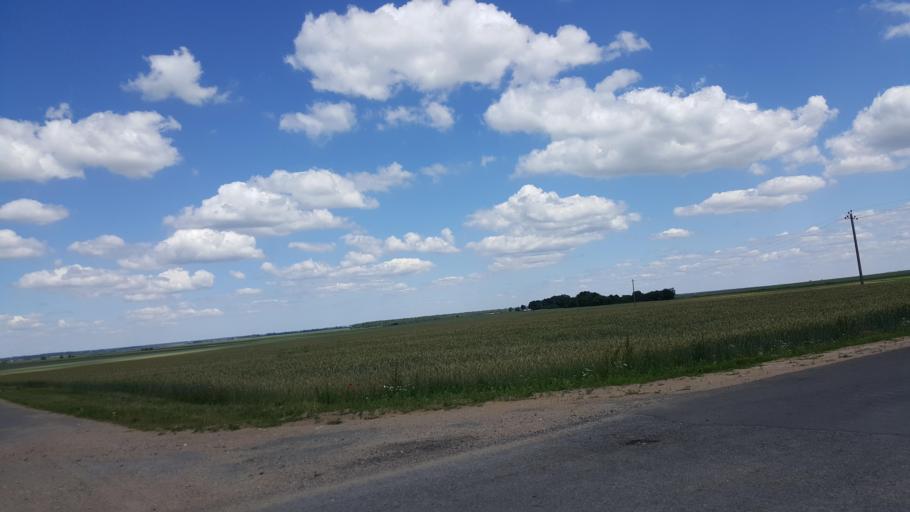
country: BY
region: Brest
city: Vysokaye
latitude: 52.4272
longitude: 23.5244
